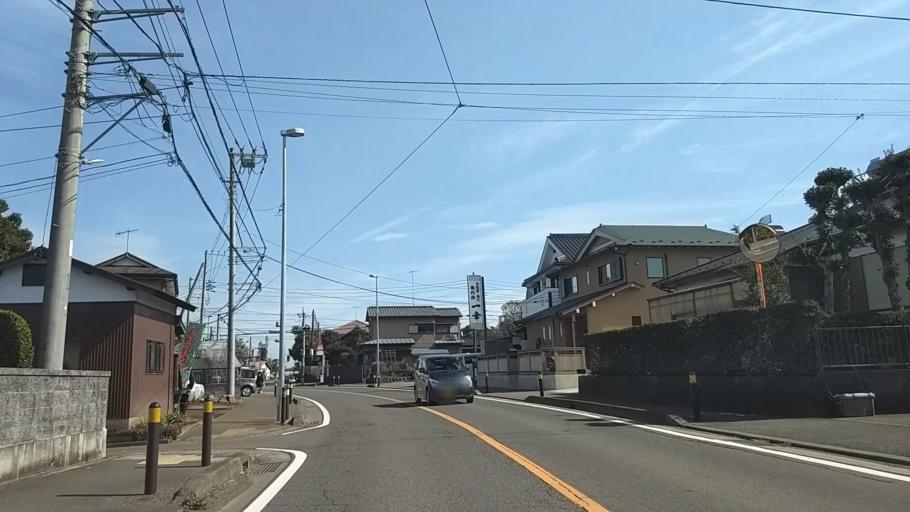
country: JP
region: Kanagawa
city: Chigasaki
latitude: 35.3862
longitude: 139.4115
